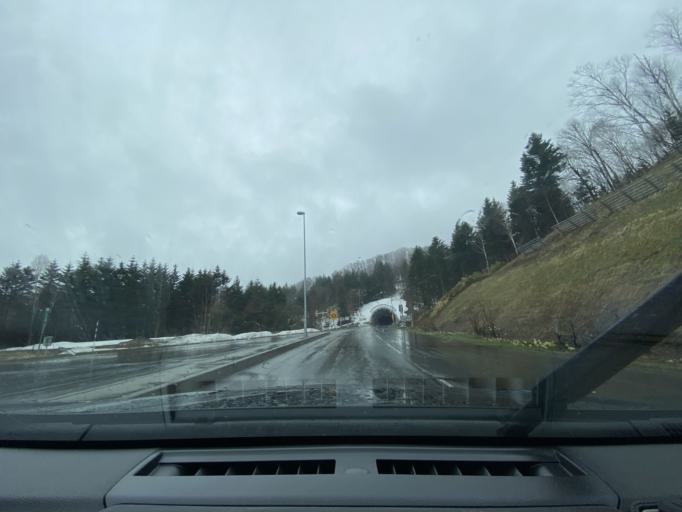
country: JP
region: Hokkaido
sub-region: Asahikawa-shi
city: Asahikawa
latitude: 43.8125
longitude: 142.2465
